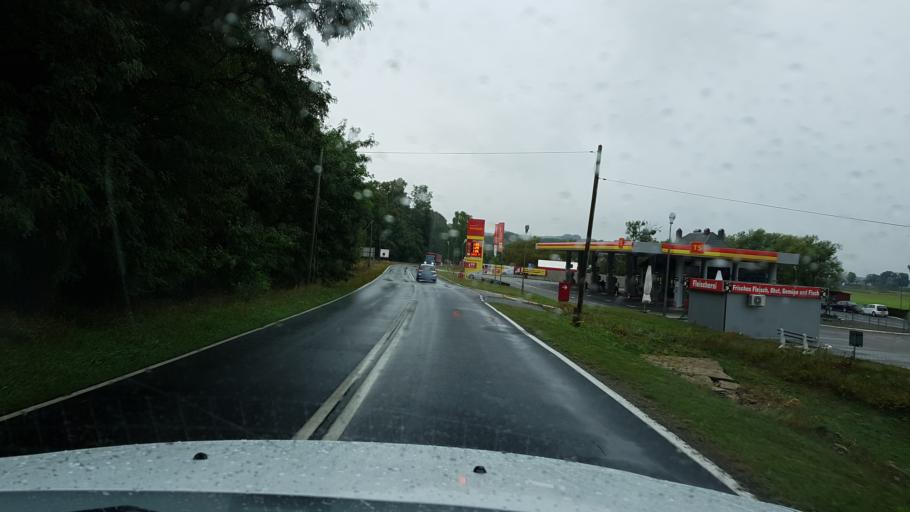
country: DE
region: Brandenburg
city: Schwedt (Oder)
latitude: 53.0372
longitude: 14.3262
